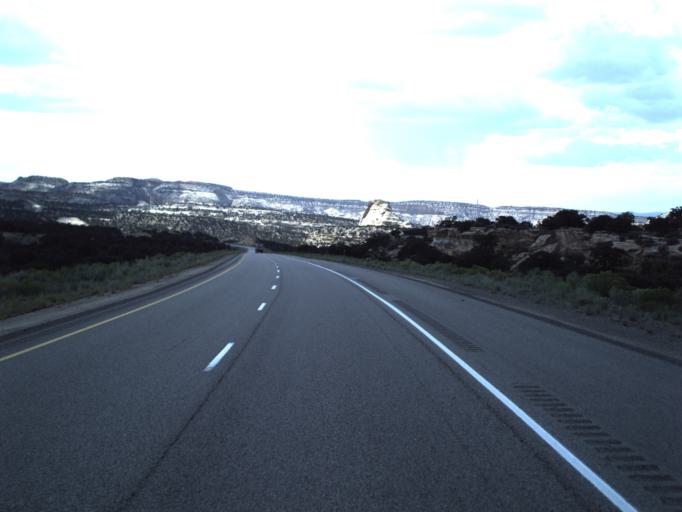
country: US
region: Utah
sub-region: Emery County
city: Ferron
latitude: 38.8649
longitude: -110.8517
